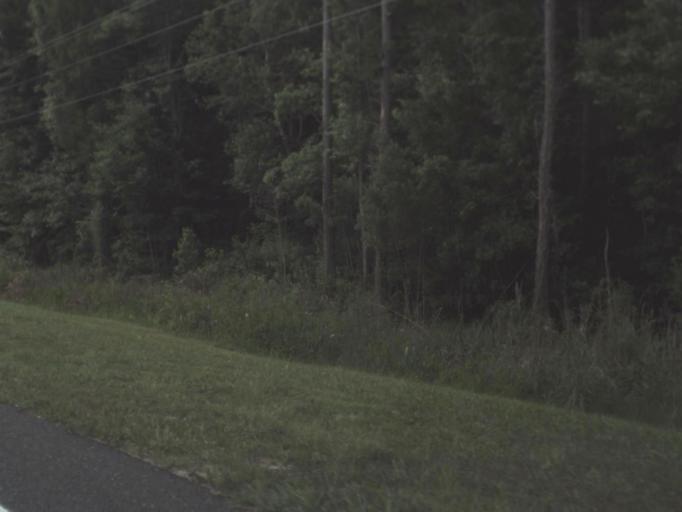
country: US
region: Florida
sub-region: Alachua County
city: Waldo
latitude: 29.7768
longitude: -82.1619
